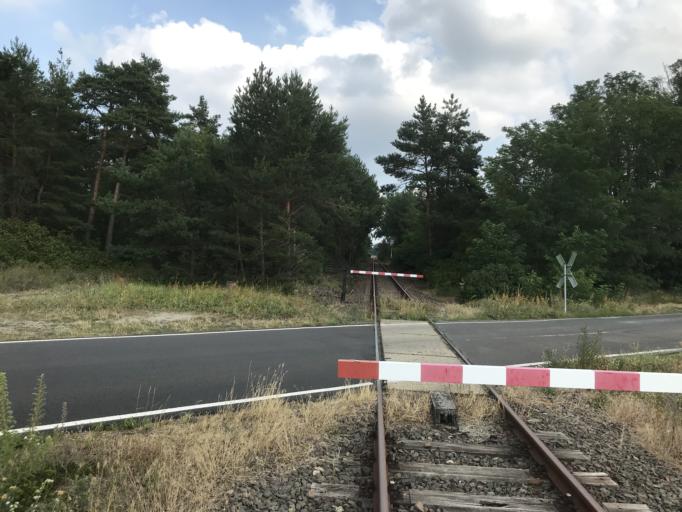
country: DE
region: Brandenburg
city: Sperenberg
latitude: 52.0804
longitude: 13.3144
